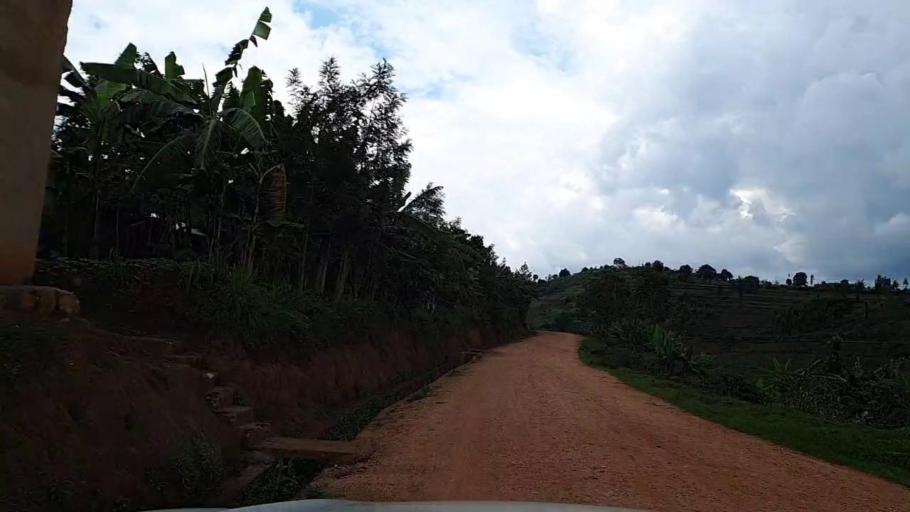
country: RW
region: Southern Province
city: Gikongoro
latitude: -2.4169
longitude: 29.6660
